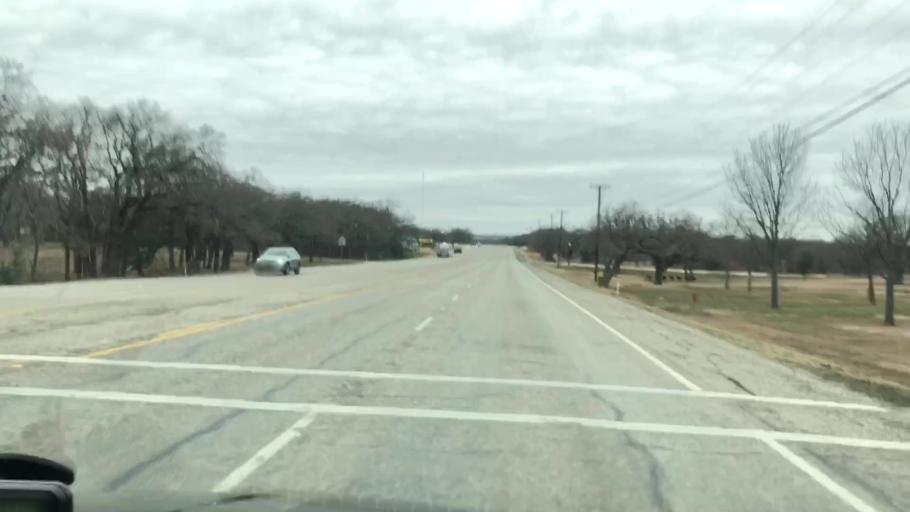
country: US
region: Texas
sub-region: Jack County
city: Jacksboro
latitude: 33.2276
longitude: -98.1707
